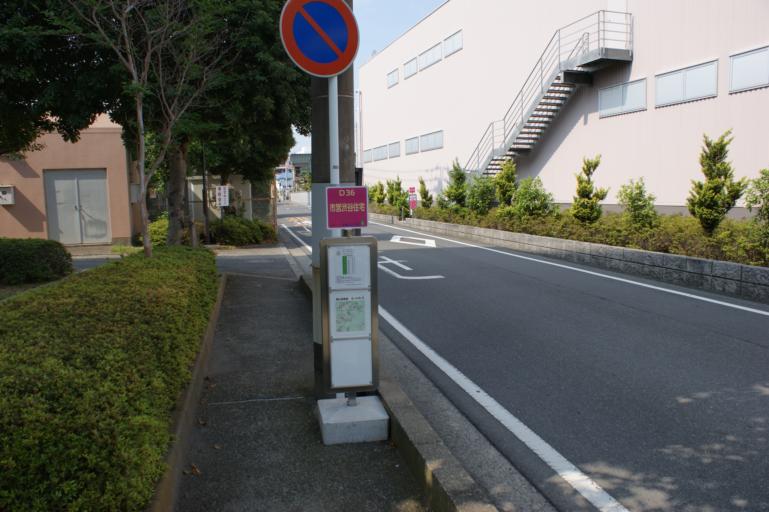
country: JP
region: Kanagawa
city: Minami-rinkan
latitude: 35.4387
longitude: 139.4657
